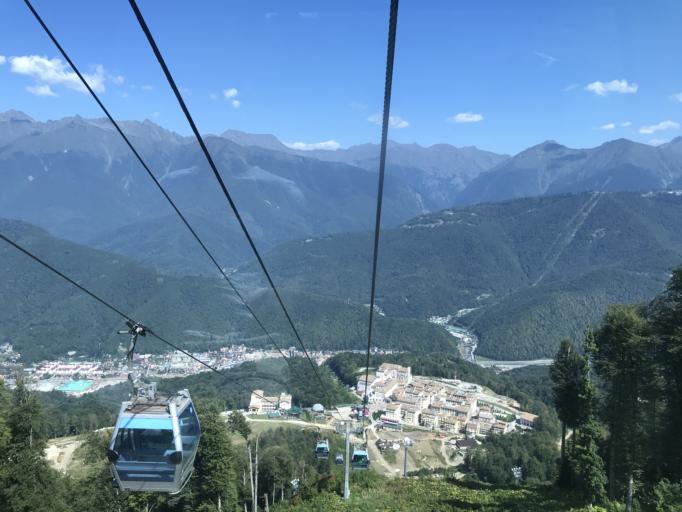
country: RU
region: Krasnodarskiy
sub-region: Sochi City
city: Krasnaya Polyana
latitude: 43.6614
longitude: 40.2528
